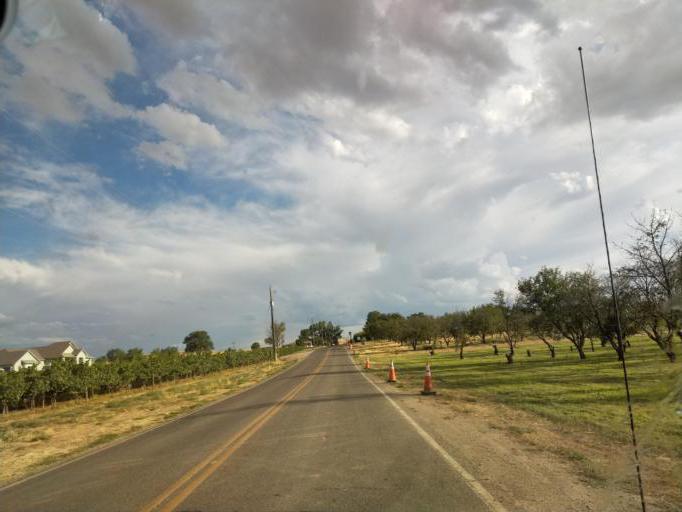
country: US
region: Colorado
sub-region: Mesa County
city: Clifton
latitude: 39.0591
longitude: -108.4133
